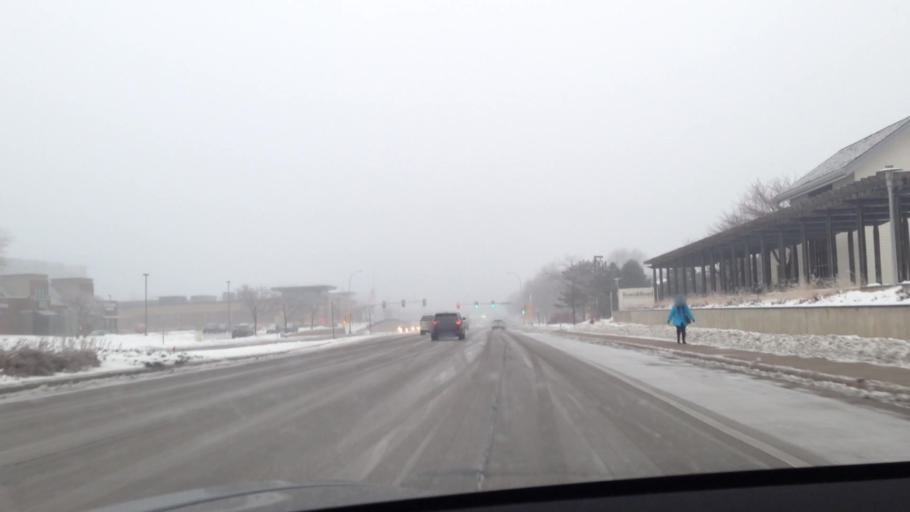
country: US
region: Minnesota
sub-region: Hennepin County
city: Edina
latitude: 44.8758
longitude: -93.3291
